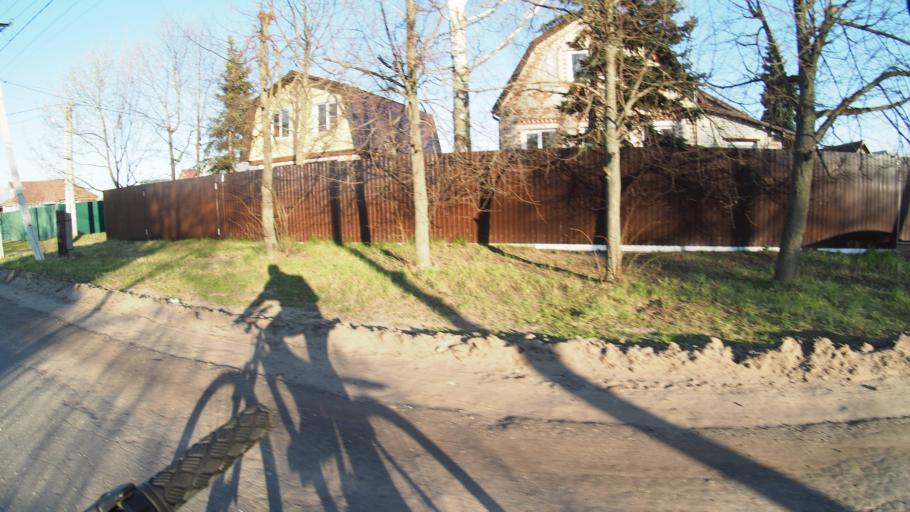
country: RU
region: Moskovskaya
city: Malyshevo
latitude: 55.4927
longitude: 38.3495
